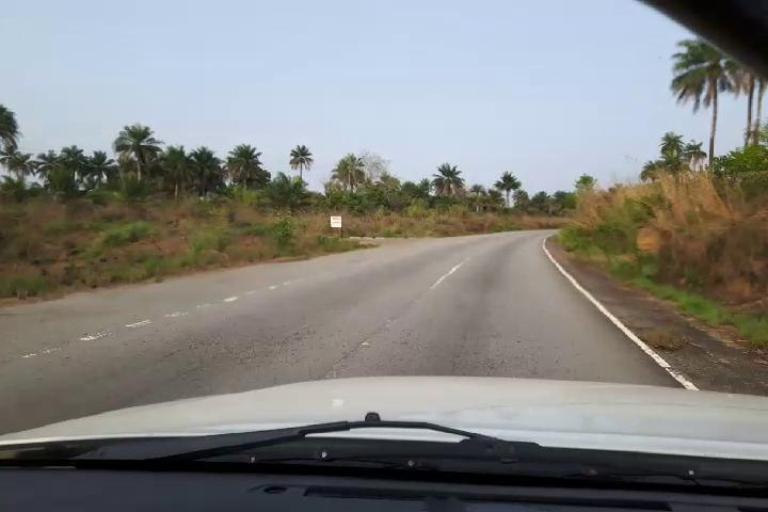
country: SL
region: Eastern Province
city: Blama
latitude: 7.9403
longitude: -11.5008
